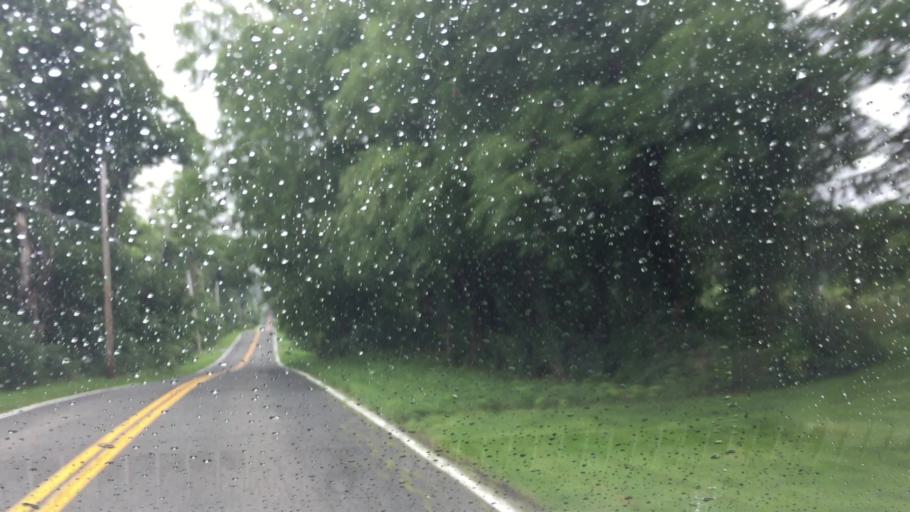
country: US
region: Massachusetts
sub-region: Berkshire County
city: West Stockbridge
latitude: 42.3038
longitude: -73.4022
